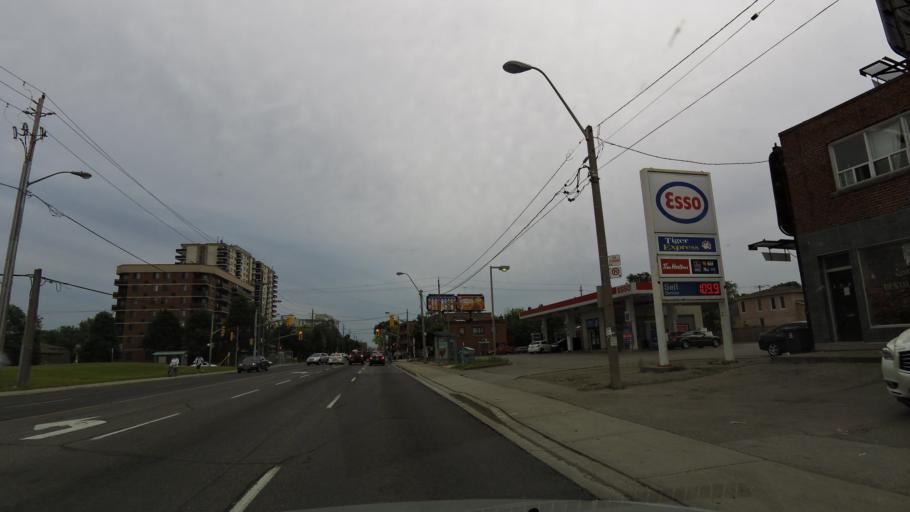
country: CA
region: Ontario
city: Etobicoke
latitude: 43.7100
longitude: -79.5058
